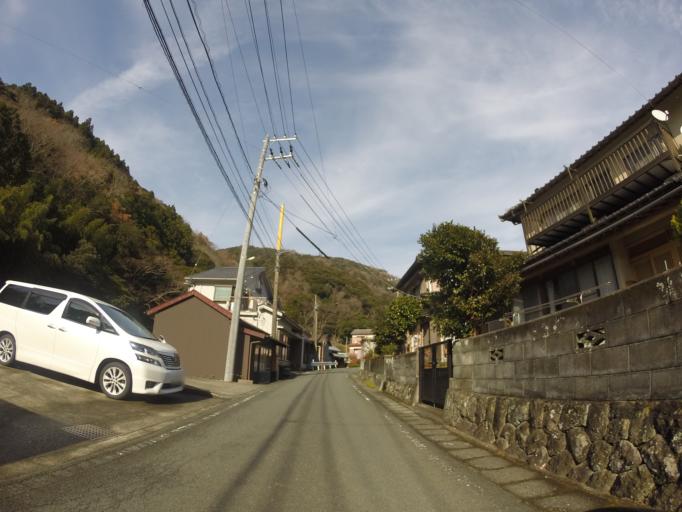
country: JP
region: Shizuoka
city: Heda
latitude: 34.8124
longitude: 138.8250
